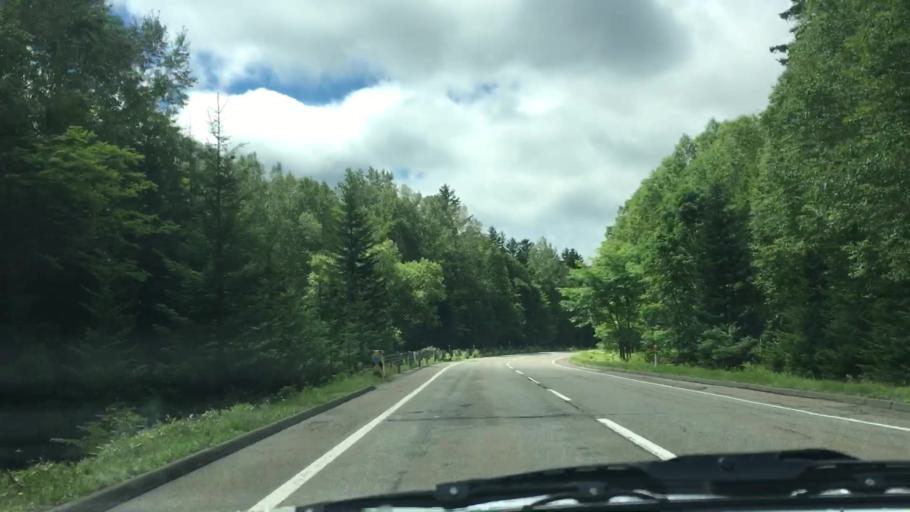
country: JP
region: Hokkaido
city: Kitami
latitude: 43.4152
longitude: 143.9736
